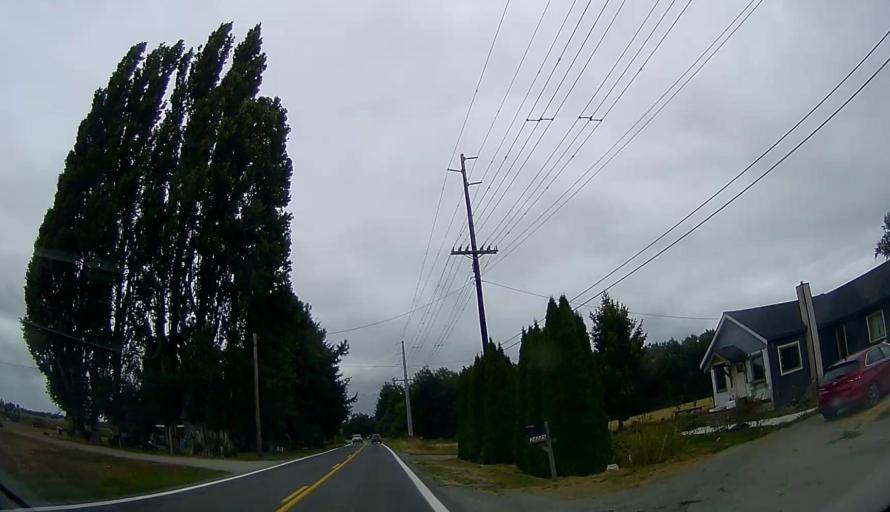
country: US
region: Washington
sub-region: Snohomish County
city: Stanwood
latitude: 48.2167
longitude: -122.3349
